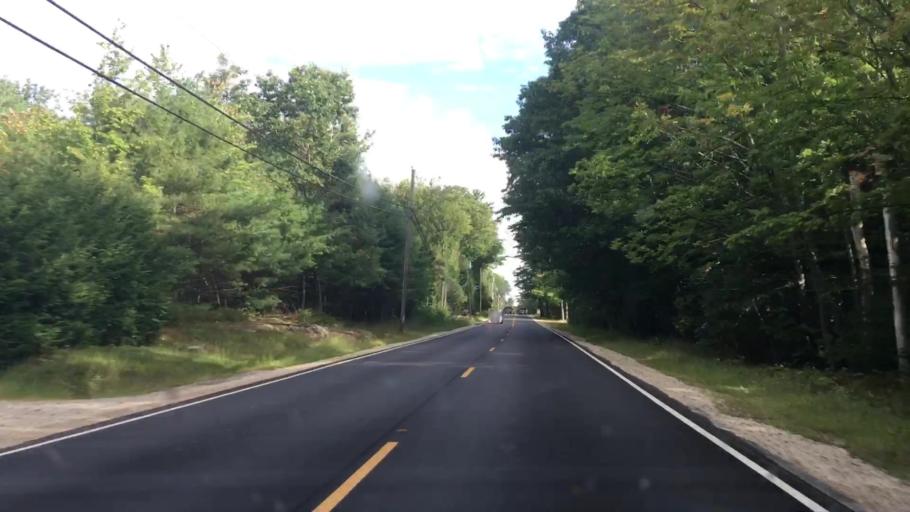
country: US
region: Maine
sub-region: Cumberland County
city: Cumberland Center
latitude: 43.7673
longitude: -70.3007
